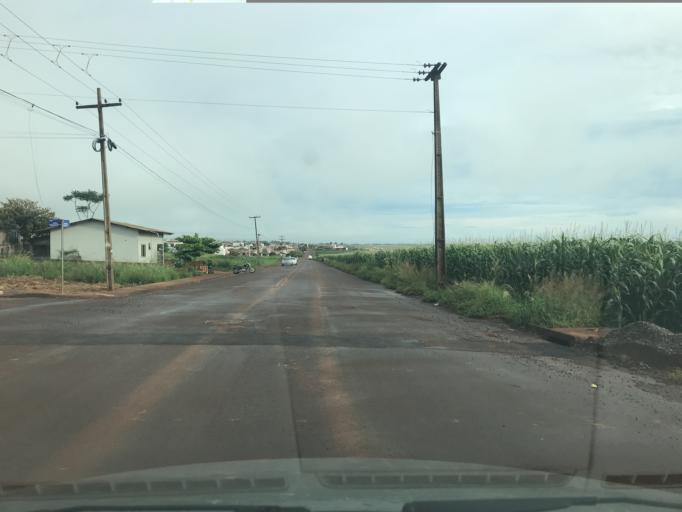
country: BR
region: Parana
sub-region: Palotina
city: Palotina
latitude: -24.3003
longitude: -53.8419
